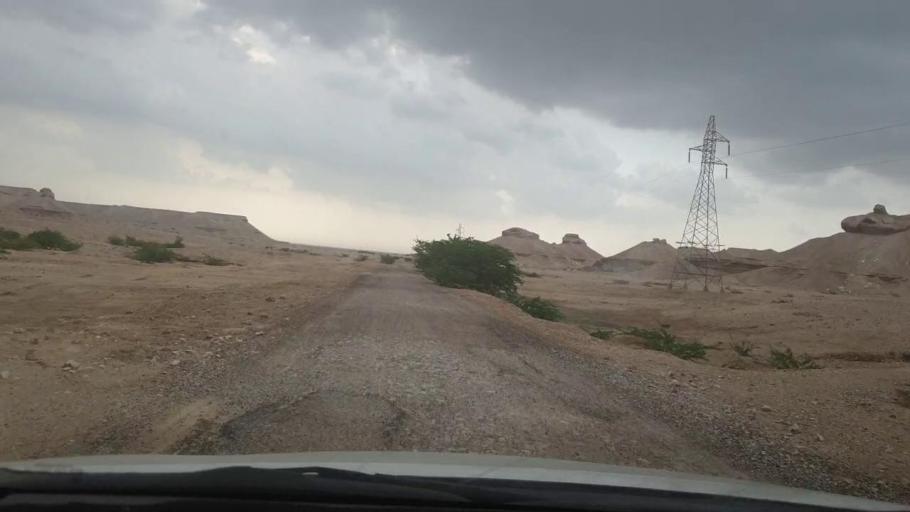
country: PK
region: Sindh
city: Khairpur
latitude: 27.4700
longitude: 68.8982
